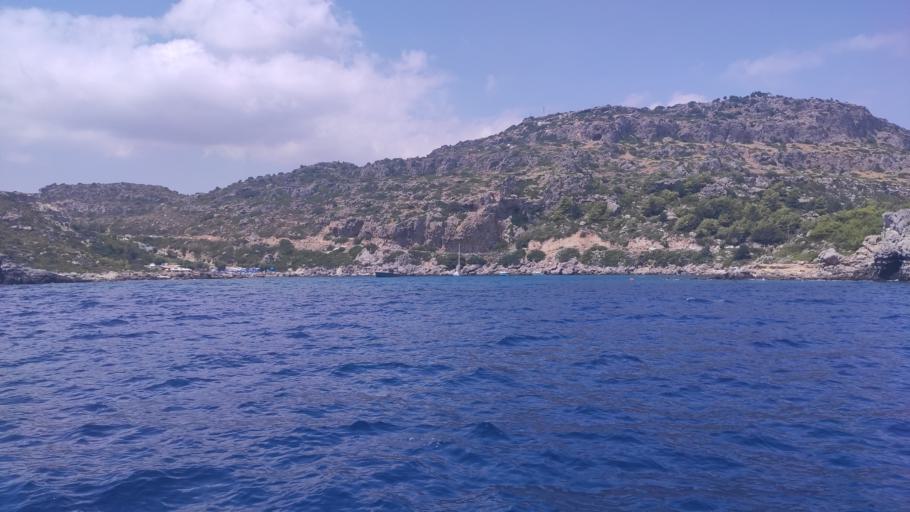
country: GR
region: South Aegean
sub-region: Nomos Dodekanisou
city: Faliraki
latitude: 36.3183
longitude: 28.2083
